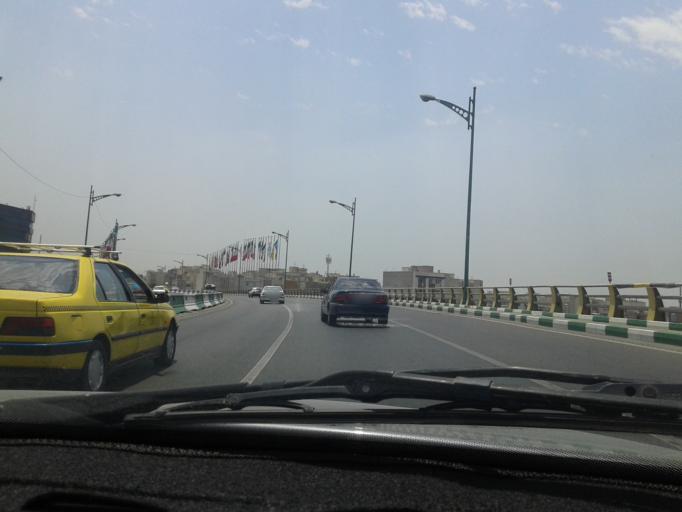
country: IR
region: Tehran
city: Tehran
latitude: 35.7193
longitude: 51.5015
